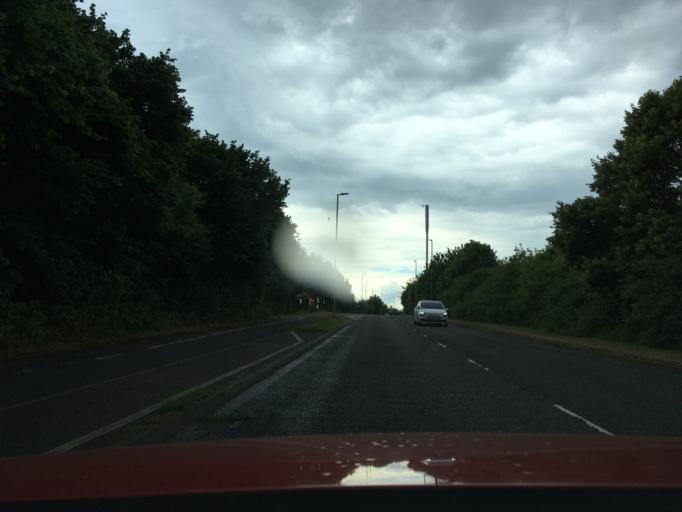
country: GB
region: England
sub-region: Gloucestershire
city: Barnwood
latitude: 51.8561
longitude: -2.2147
